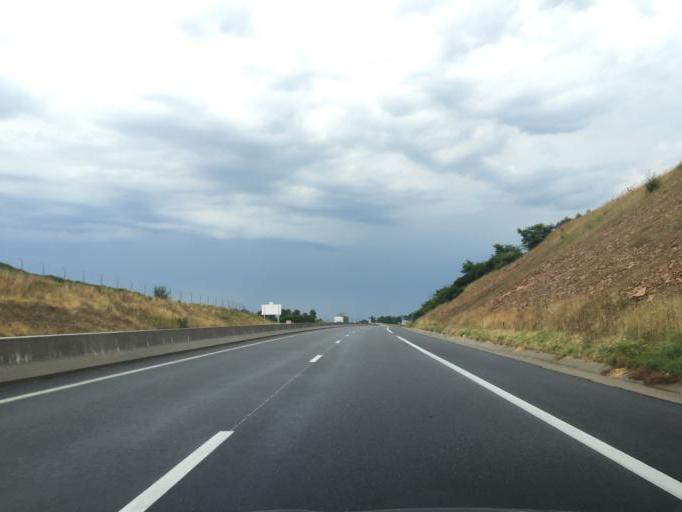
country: FR
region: Rhone-Alpes
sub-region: Departement de la Loire
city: La Pacaudiere
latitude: 46.2202
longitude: 3.7677
